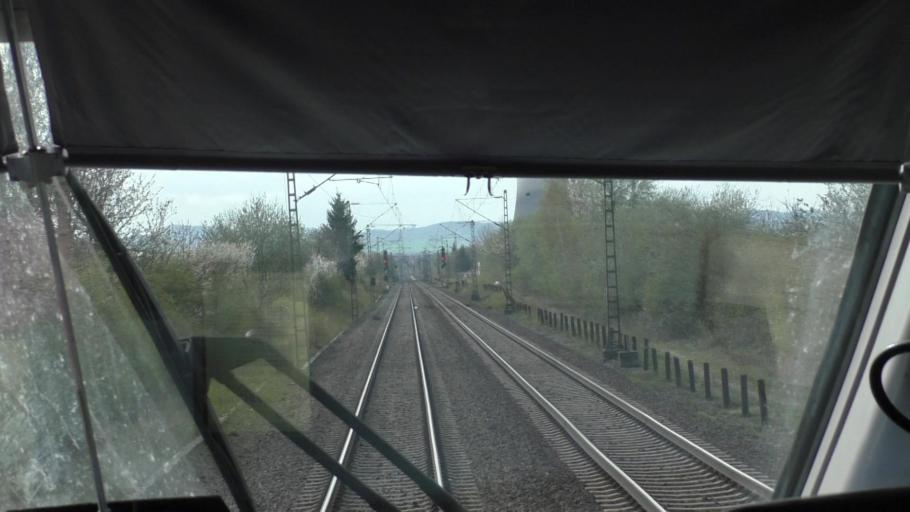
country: DE
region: Rheinland-Pfalz
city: Urmitz
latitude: 50.3999
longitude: 7.5248
